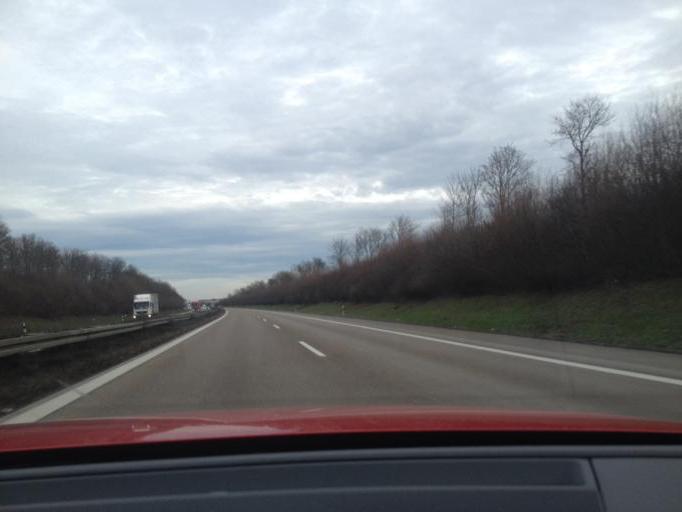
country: DE
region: Baden-Wuerttemberg
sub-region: Regierungsbezirk Stuttgart
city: Braunsbach
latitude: 49.1734
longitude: 9.8057
